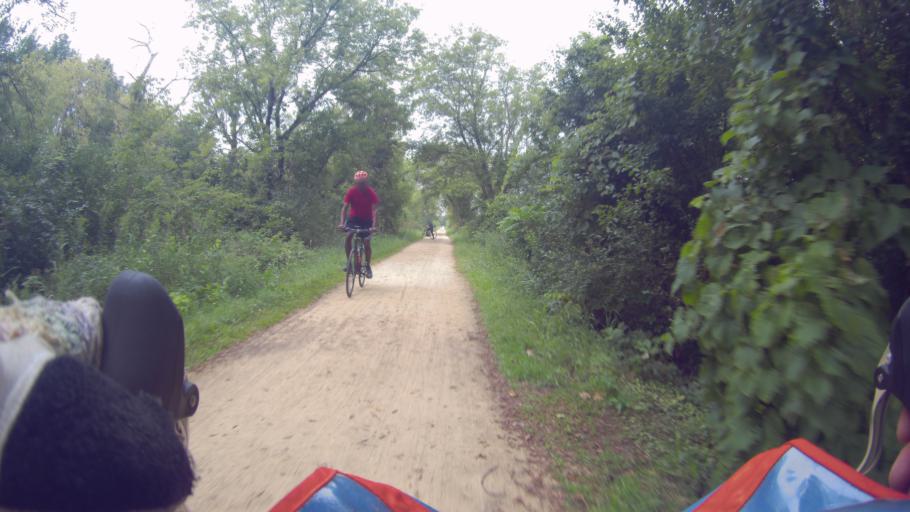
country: US
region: Wisconsin
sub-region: Dane County
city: Verona
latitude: 42.9920
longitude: -89.5151
